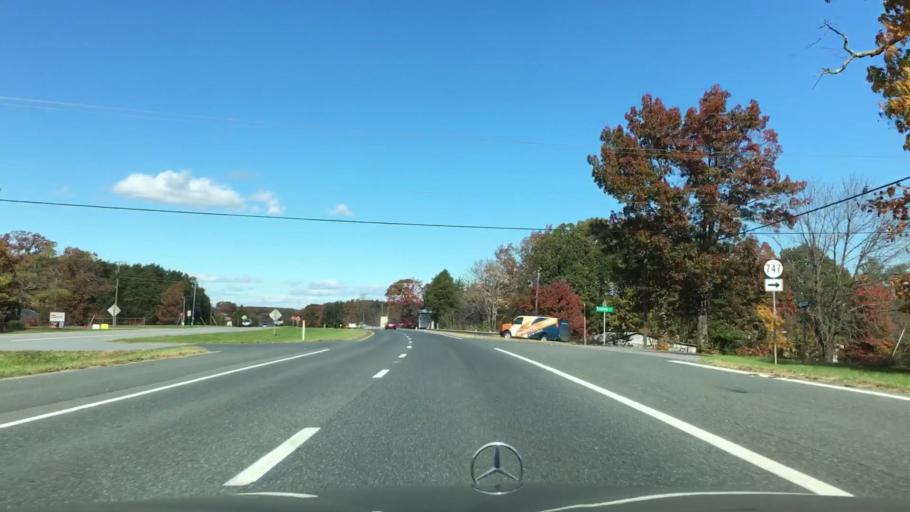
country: US
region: Virginia
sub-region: Campbell County
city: Rustburg
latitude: 37.2359
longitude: -79.1855
